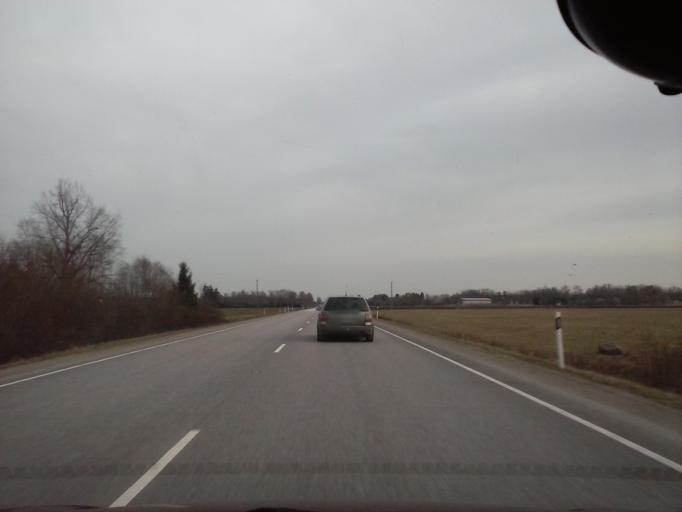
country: EE
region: Jaervamaa
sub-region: Paide linn
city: Paide
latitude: 58.8024
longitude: 25.7578
